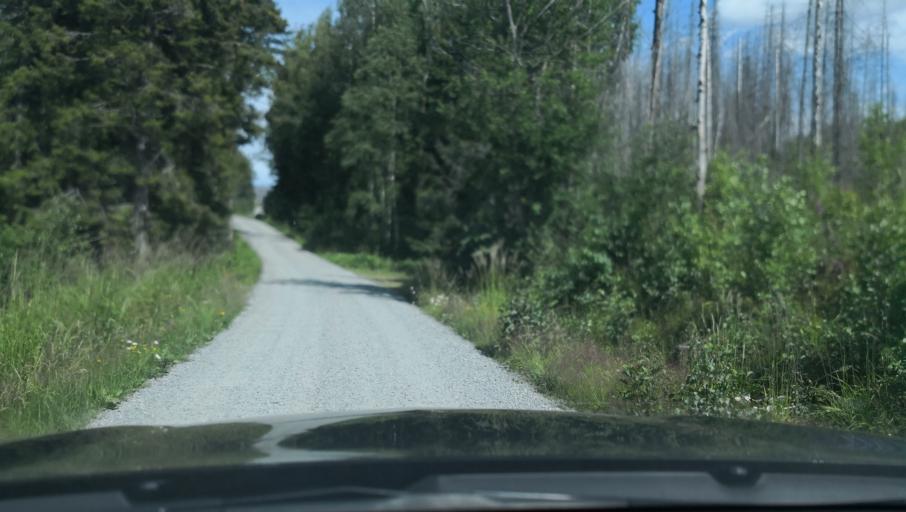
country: SE
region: Vaestmanland
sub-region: Surahammars Kommun
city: Ramnas
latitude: 59.8971
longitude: 16.1052
